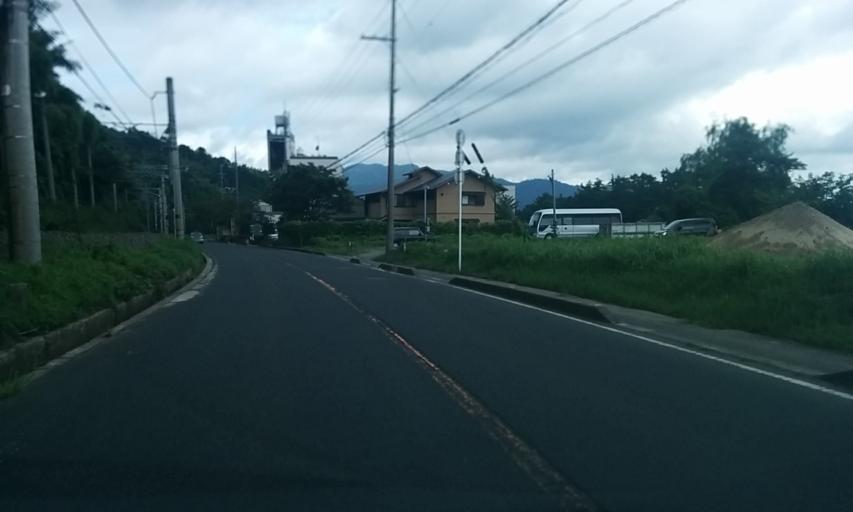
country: JP
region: Kyoto
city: Miyazu
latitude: 35.5503
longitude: 135.1873
